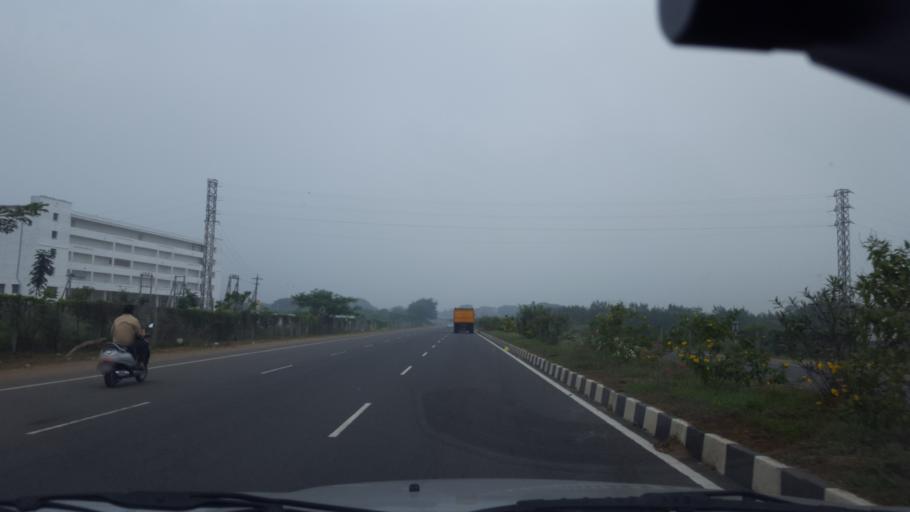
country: IN
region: Andhra Pradesh
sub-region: Prakasam
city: Addanki
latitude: 15.8139
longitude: 80.0424
